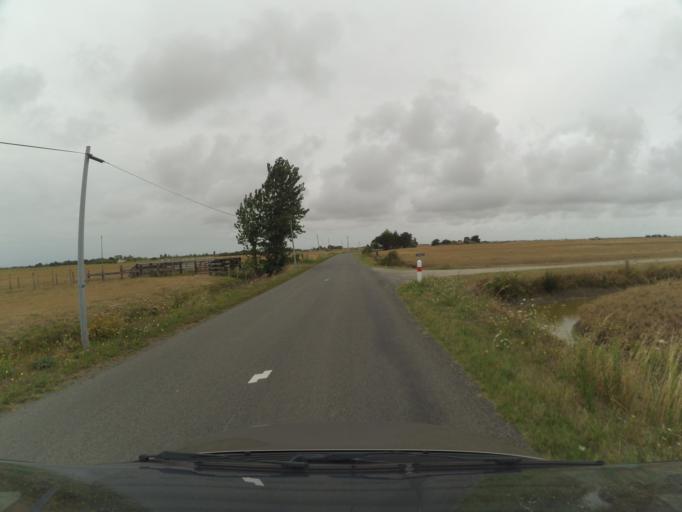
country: FR
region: Pays de la Loire
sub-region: Departement de la Vendee
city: Saint-Urbain
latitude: 46.8748
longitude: -2.0455
